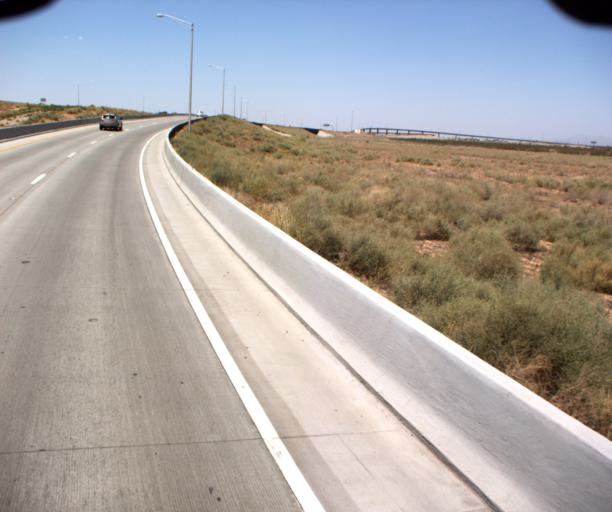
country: US
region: Arizona
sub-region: Maricopa County
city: Queen Creek
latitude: 33.3189
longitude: -111.6385
